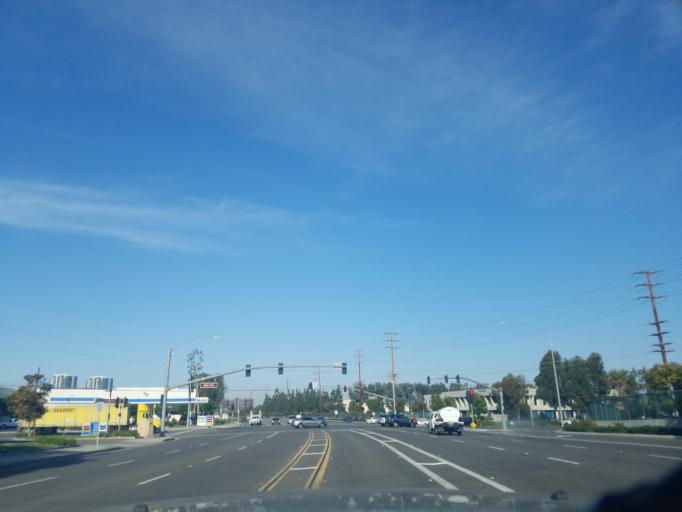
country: US
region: California
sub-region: Orange County
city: Irvine
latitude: 33.6933
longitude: -117.8544
